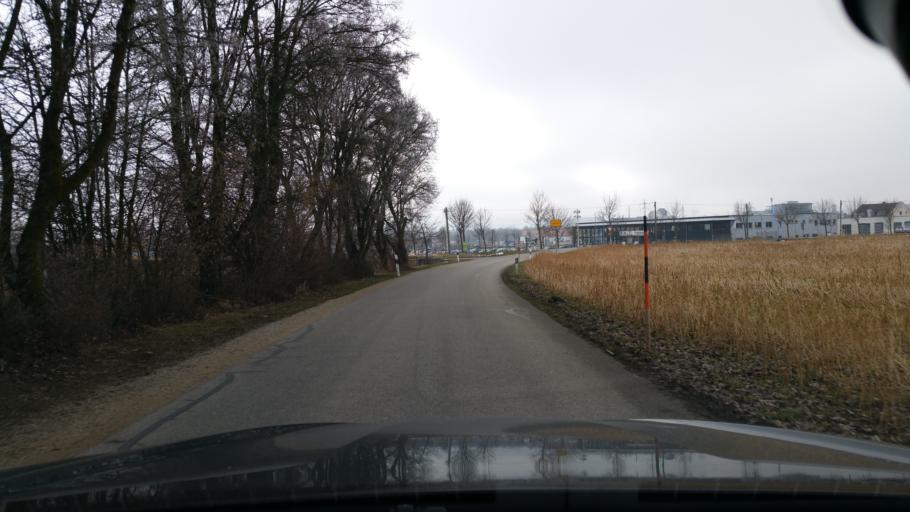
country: DE
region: Bavaria
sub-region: Lower Bavaria
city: Ergolding
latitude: 48.5659
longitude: 12.1370
